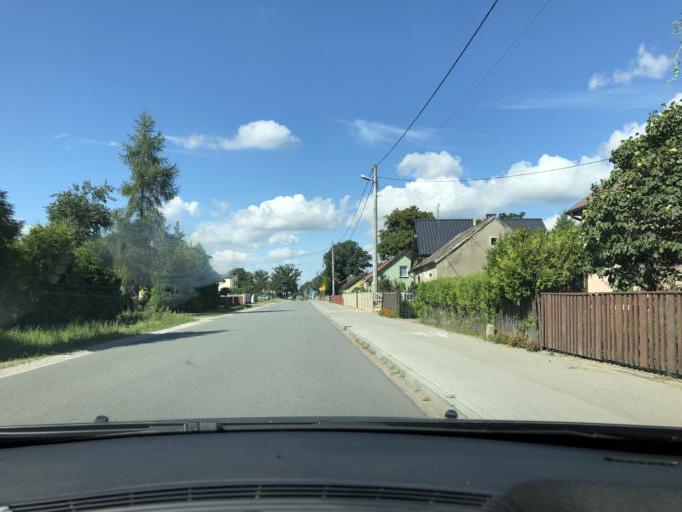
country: PL
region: Lodz Voivodeship
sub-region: Powiat wieruszowski
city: Czastary
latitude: 51.2419
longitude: 18.3200
